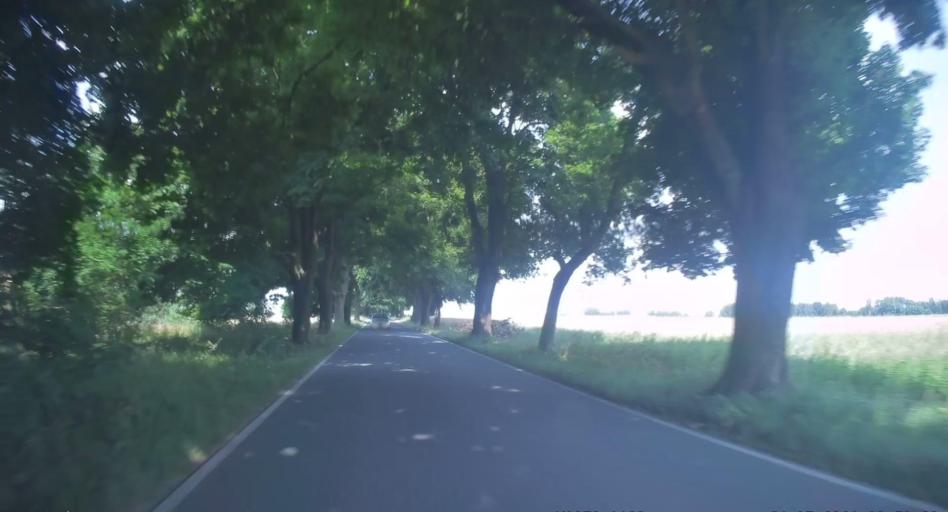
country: PL
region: Lodz Voivodeship
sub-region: Powiat tomaszowski
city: Lubochnia
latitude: 51.5629
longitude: 20.1220
